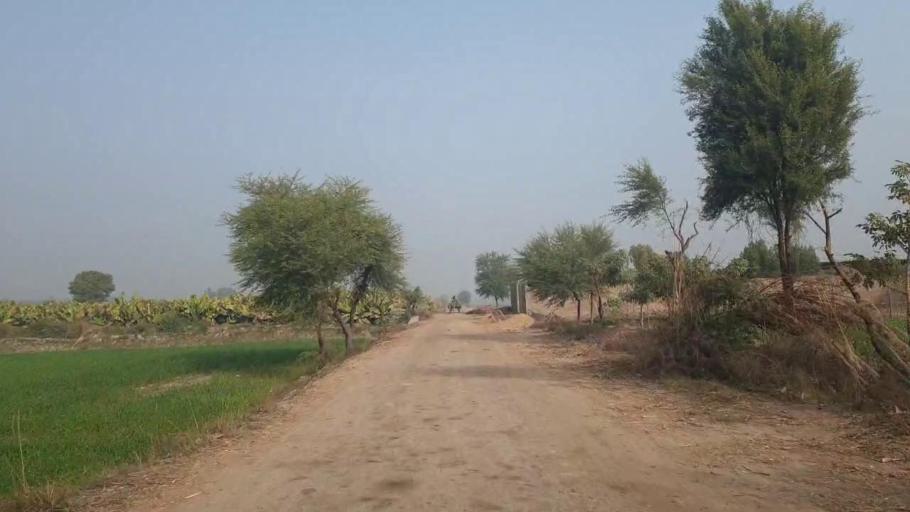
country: PK
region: Sindh
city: Tando Adam
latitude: 25.8109
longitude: 68.6153
